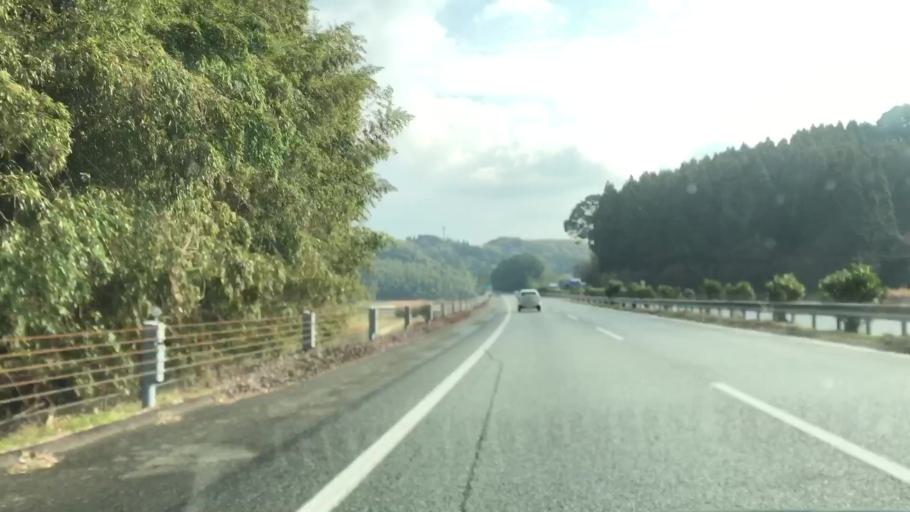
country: JP
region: Kumamoto
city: Yamaga
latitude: 33.0310
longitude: 130.5741
